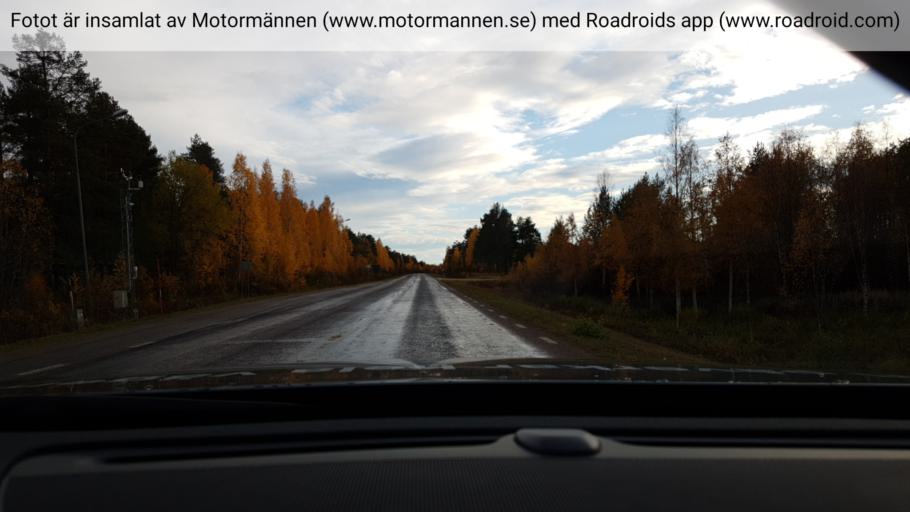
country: SE
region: Norrbotten
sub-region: Pajala Kommun
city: Pajala
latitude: 67.1587
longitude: 22.6315
